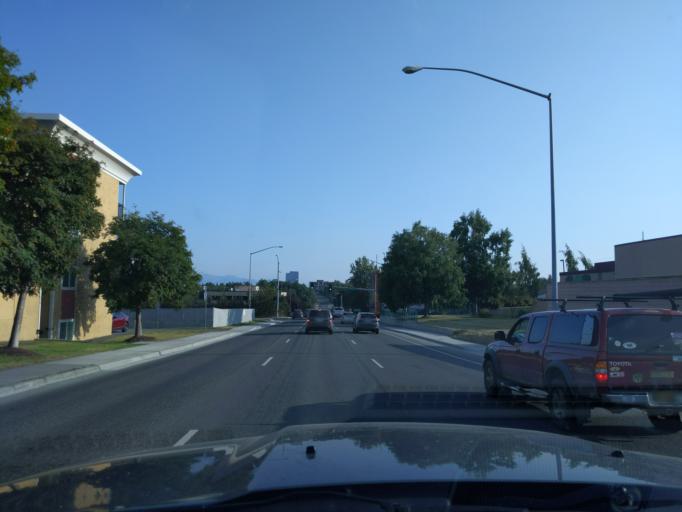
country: US
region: Alaska
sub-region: Anchorage Municipality
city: Anchorage
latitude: 61.2086
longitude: -149.8873
